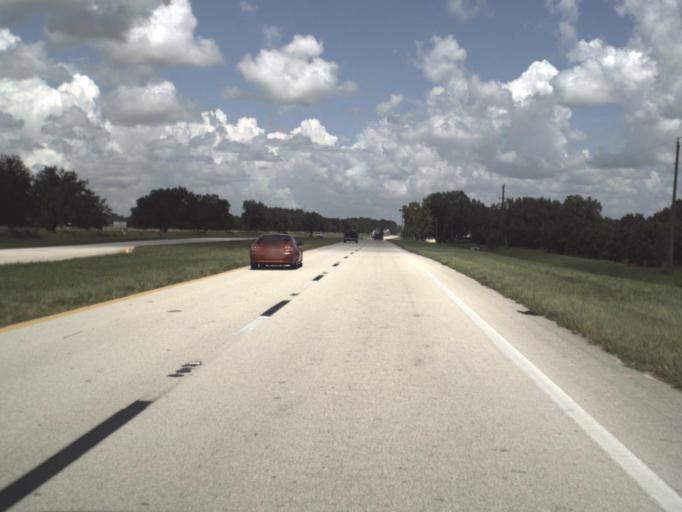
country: US
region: Florida
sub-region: Polk County
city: Fort Meade
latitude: 27.7304
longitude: -81.8013
